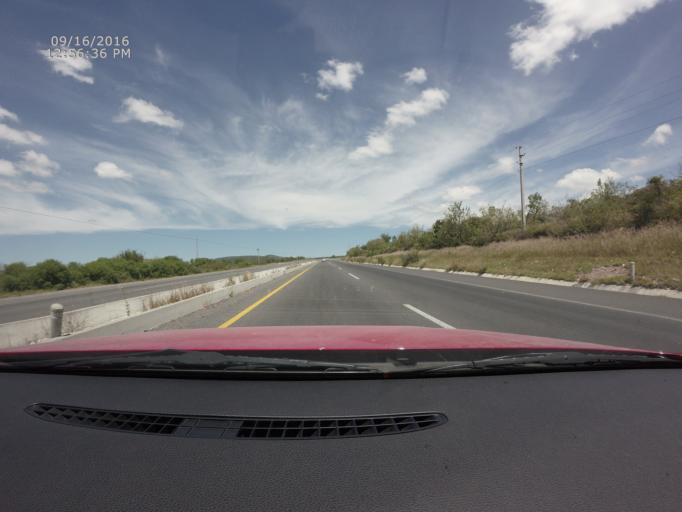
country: MX
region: Queretaro
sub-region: Colon
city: Purisima de Cubos (La Purisima)
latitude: 20.6566
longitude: -100.0994
